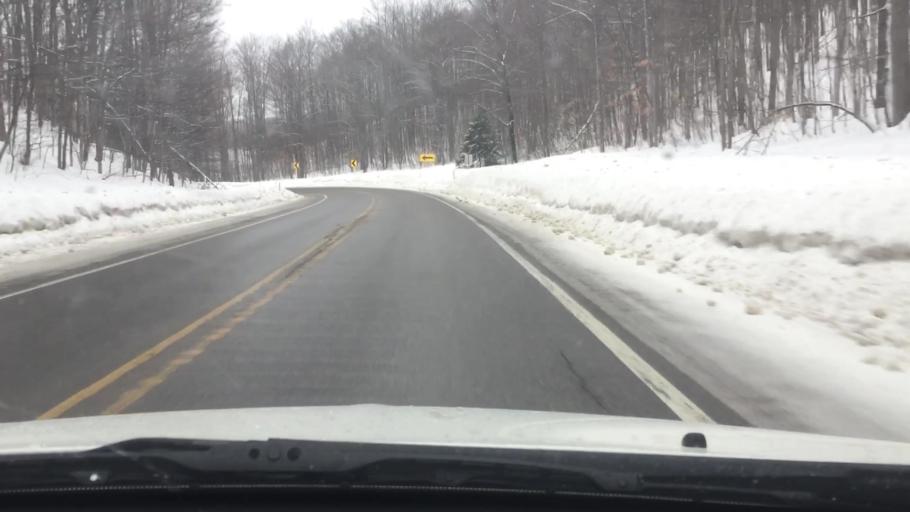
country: US
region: Michigan
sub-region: Charlevoix County
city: Boyne City
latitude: 45.0805
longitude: -84.9122
